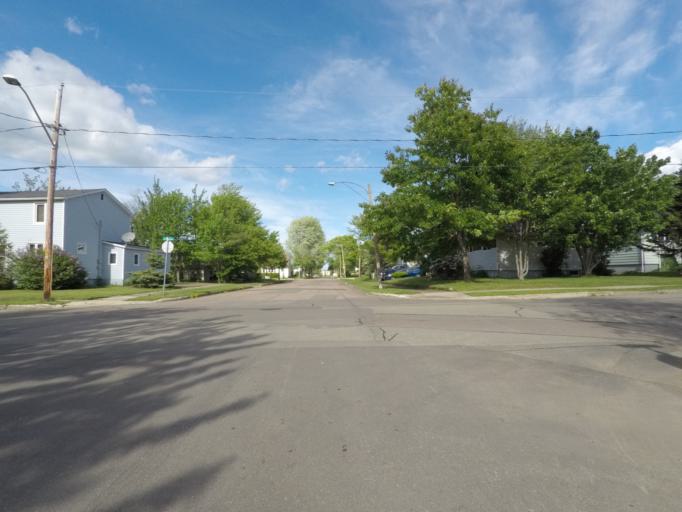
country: CA
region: New Brunswick
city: Moncton
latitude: 46.1028
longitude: -64.8221
